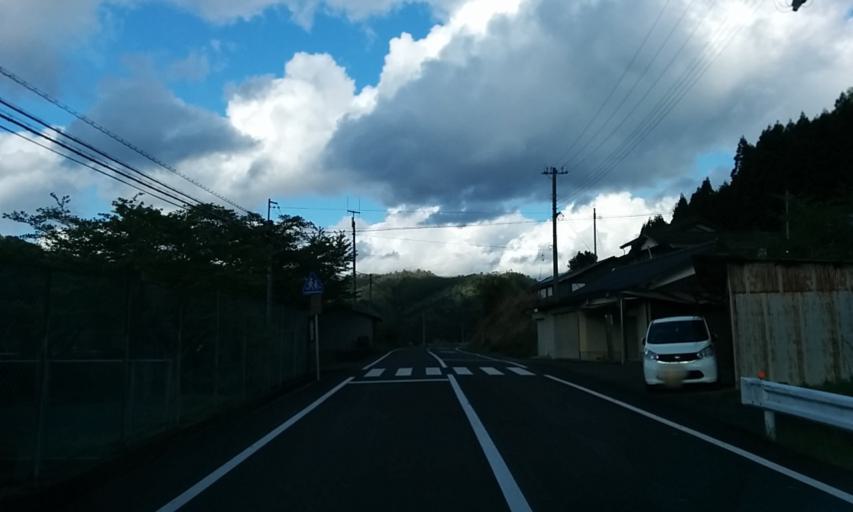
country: JP
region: Kyoto
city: Ayabe
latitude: 35.2710
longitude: 135.3548
